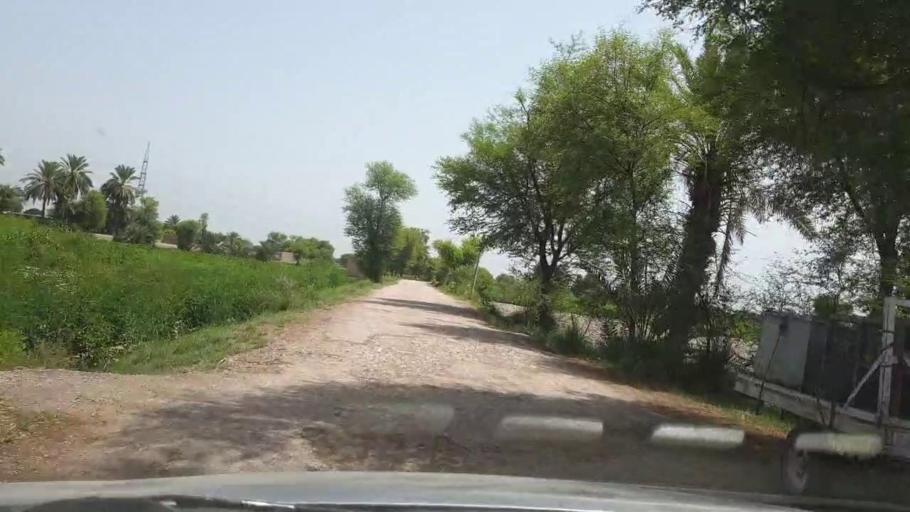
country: PK
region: Sindh
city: Pano Aqil
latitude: 27.8290
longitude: 69.2122
